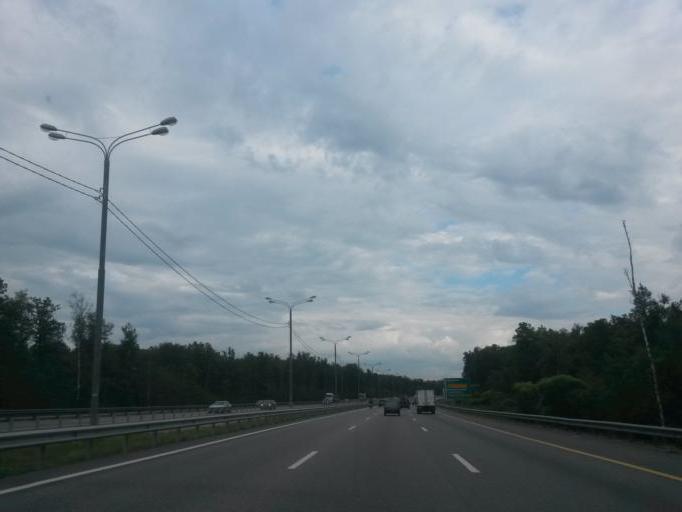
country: RU
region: Moskovskaya
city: Vostryakovo
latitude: 55.3606
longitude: 37.7944
